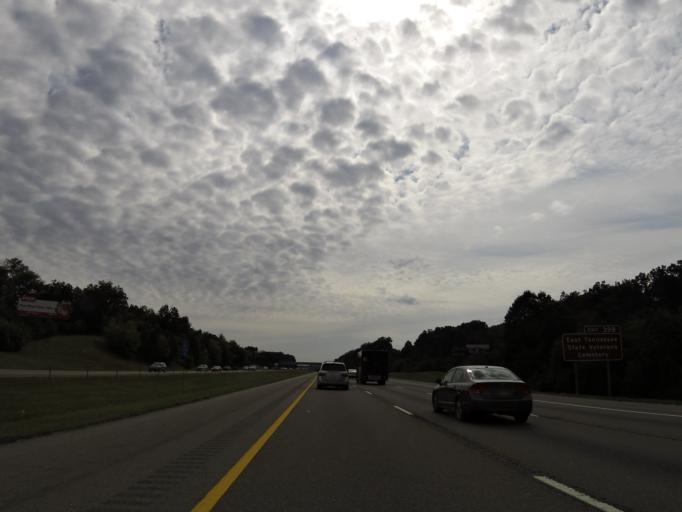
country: US
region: Tennessee
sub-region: Knox County
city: Mascot
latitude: 36.0045
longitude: -83.7943
